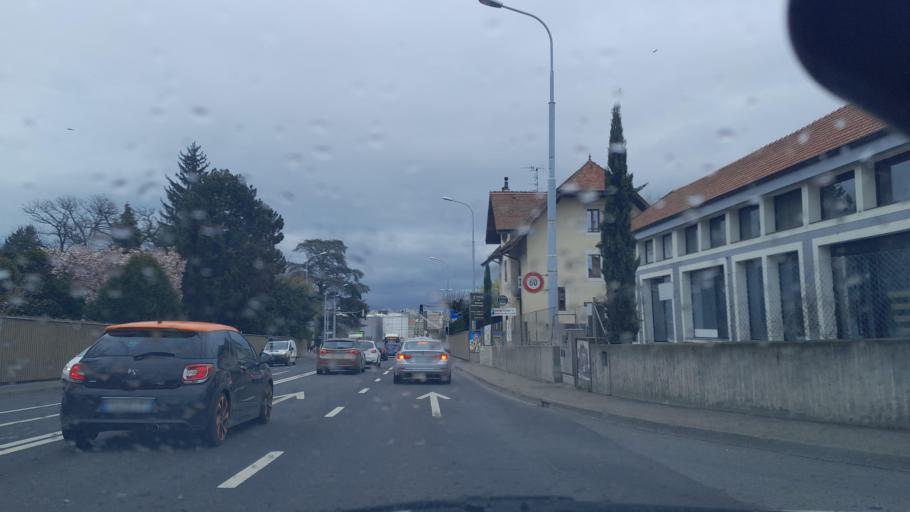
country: CH
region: Geneva
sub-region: Geneva
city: Vernier
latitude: 46.2195
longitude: 6.0918
